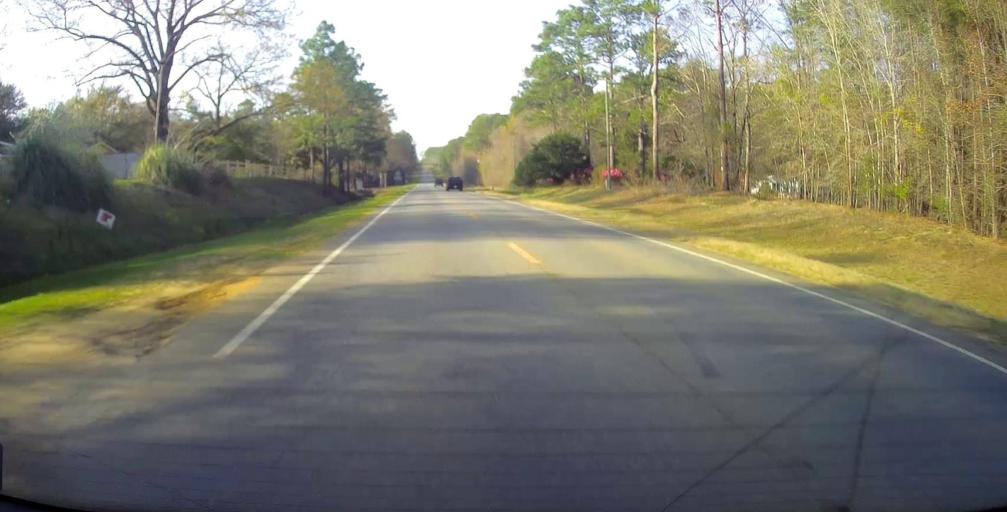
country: US
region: Georgia
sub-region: Toombs County
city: Lyons
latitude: 32.1649
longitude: -82.2717
